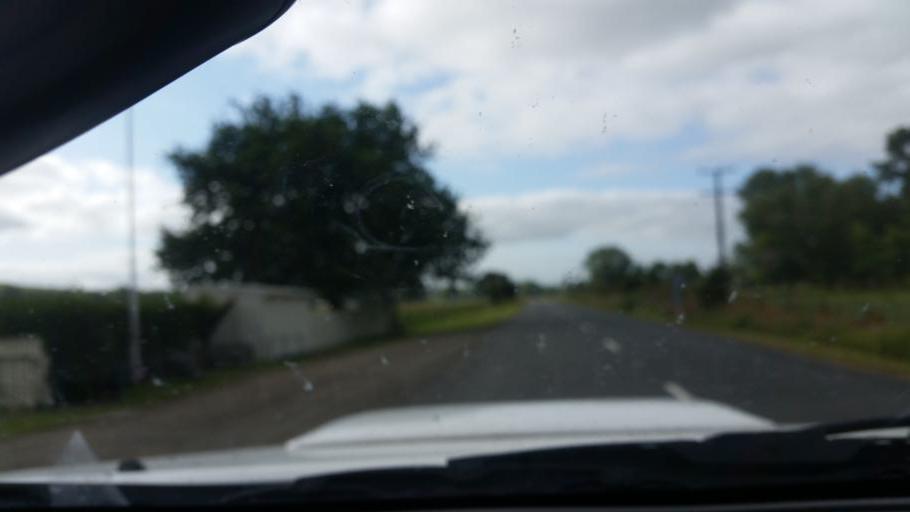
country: NZ
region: Northland
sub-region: Kaipara District
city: Dargaville
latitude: -35.8316
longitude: 173.8416
